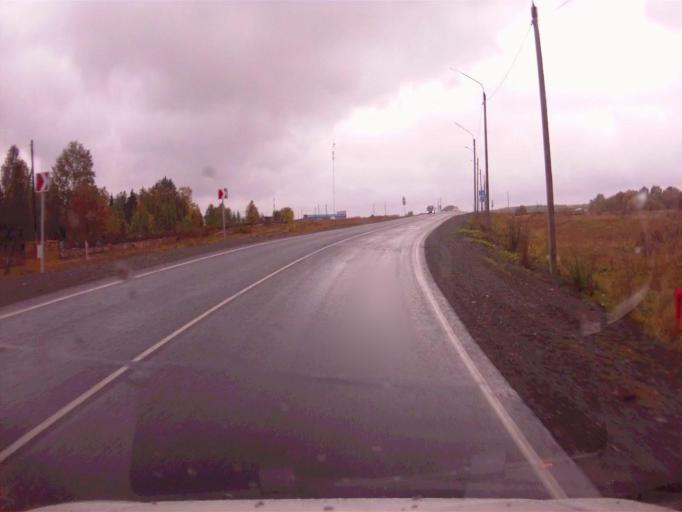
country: RU
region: Chelyabinsk
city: Tayginka
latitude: 55.4972
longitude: 60.6432
